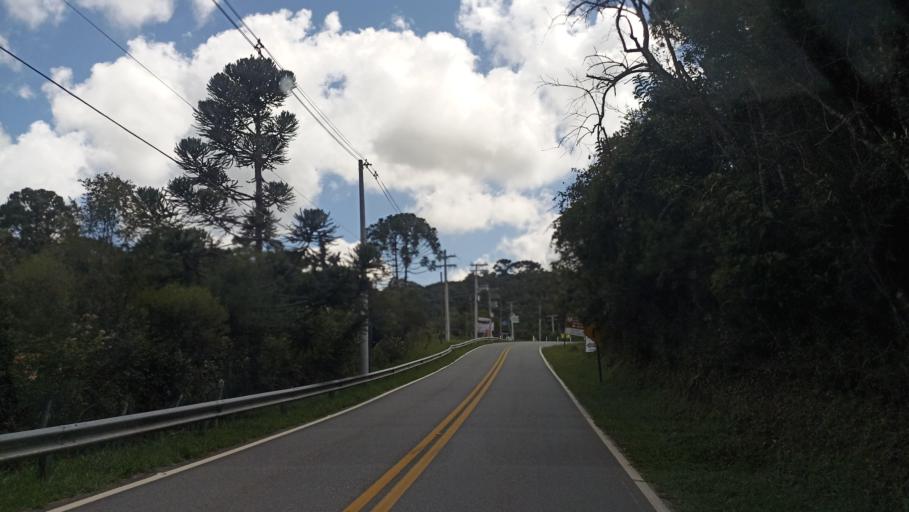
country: BR
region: Sao Paulo
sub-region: Cunha
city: Cunha
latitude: -23.1407
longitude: -44.9255
